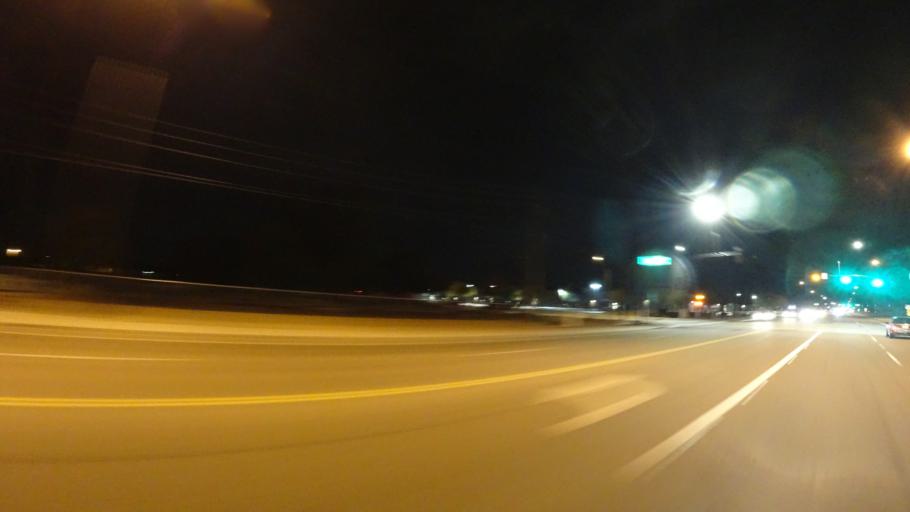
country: US
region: Arizona
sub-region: Maricopa County
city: Gilbert
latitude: 33.2632
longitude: -111.7462
